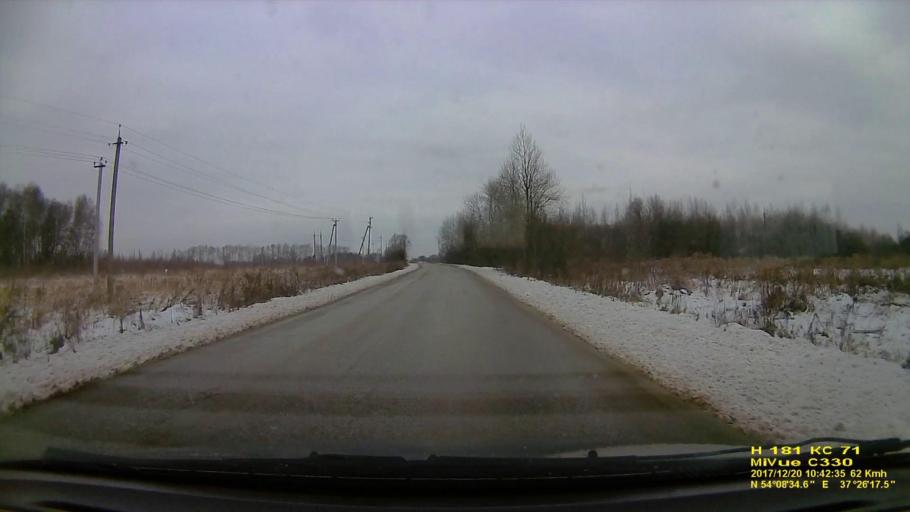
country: RU
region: Tula
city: Kosaya Gora
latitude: 54.1430
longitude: 37.4382
